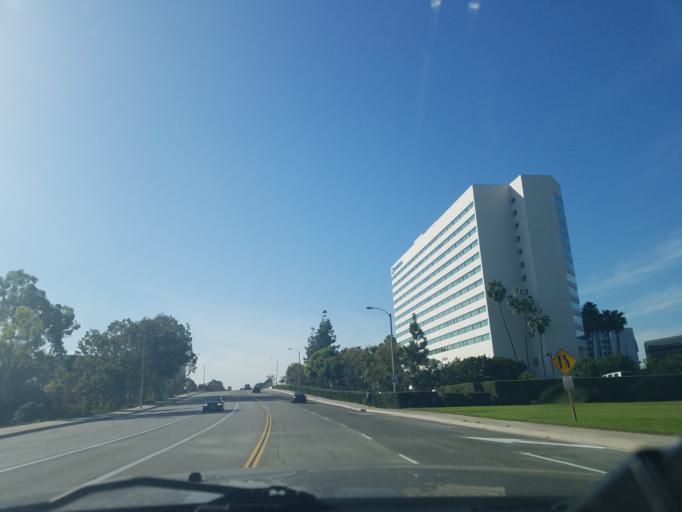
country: US
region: California
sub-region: Orange County
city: Irvine
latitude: 33.6823
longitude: -117.8496
